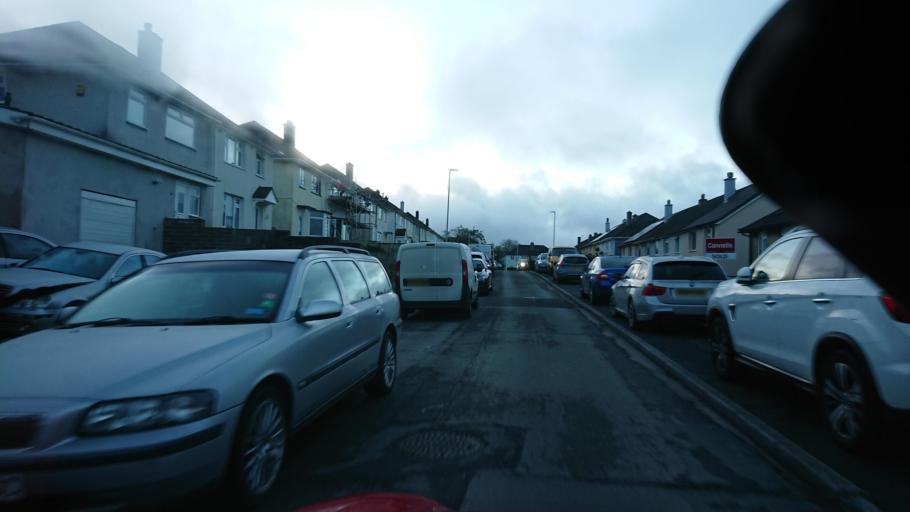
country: GB
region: England
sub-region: Cornwall
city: Torpoint
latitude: 50.4200
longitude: -4.1729
